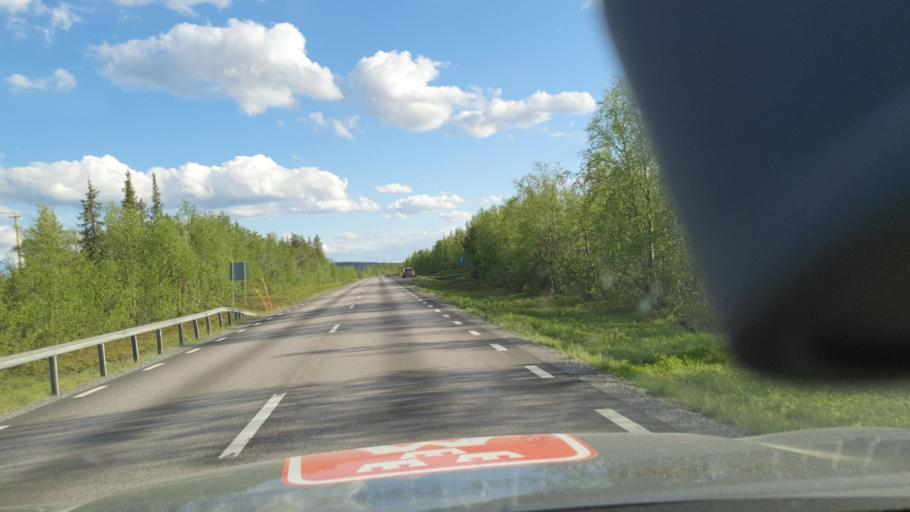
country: SE
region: Norrbotten
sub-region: Gallivare Kommun
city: Malmberget
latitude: 67.5287
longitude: 21.1502
